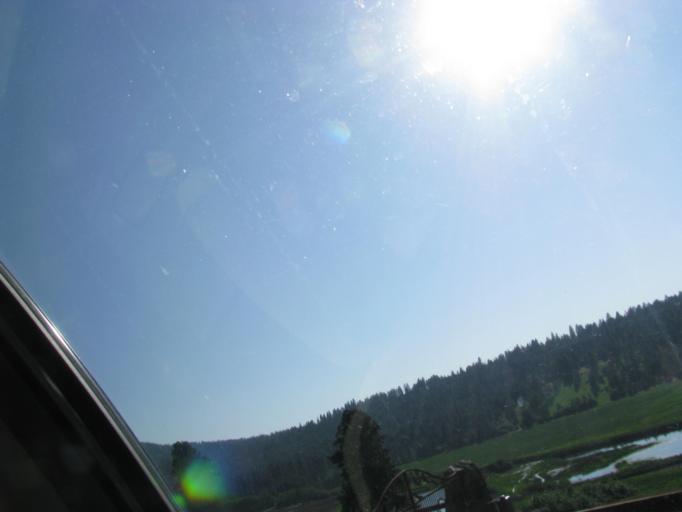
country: US
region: Washington
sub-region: Spokane County
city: Liberty Lake
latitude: 47.6099
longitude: -117.1214
